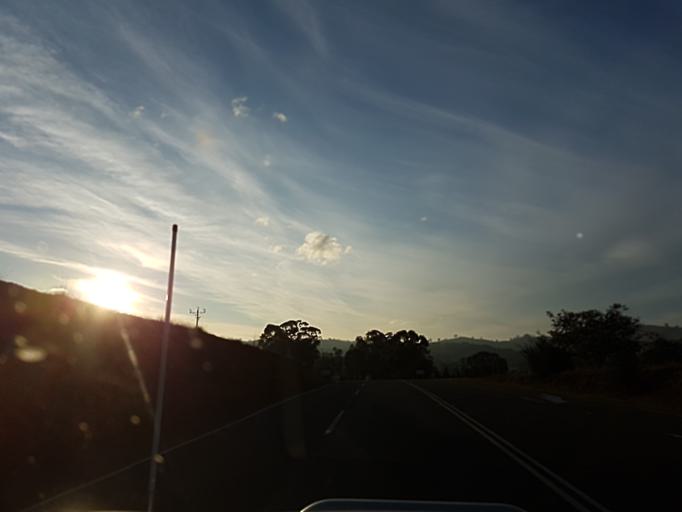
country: AU
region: Victoria
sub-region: Murrindindi
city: Alexandra
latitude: -37.1842
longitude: 145.6976
